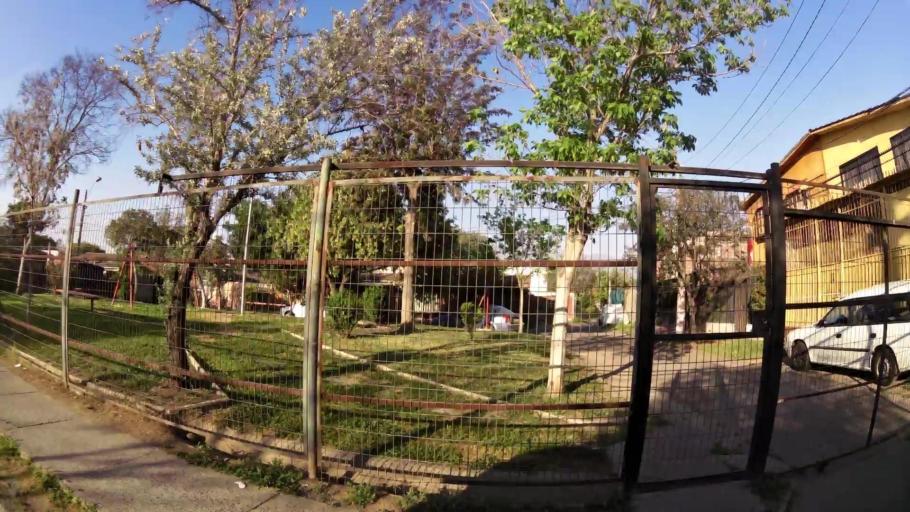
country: CL
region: Santiago Metropolitan
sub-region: Provincia de Santiago
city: La Pintana
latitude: -33.5548
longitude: -70.6184
